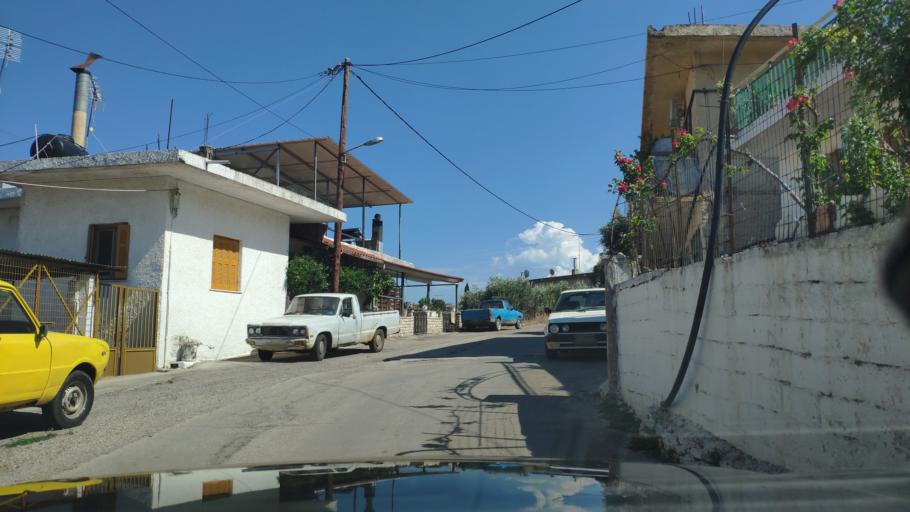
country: GR
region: West Greece
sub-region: Nomos Aitolias kai Akarnanias
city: Katouna
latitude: 38.7908
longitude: 21.1154
